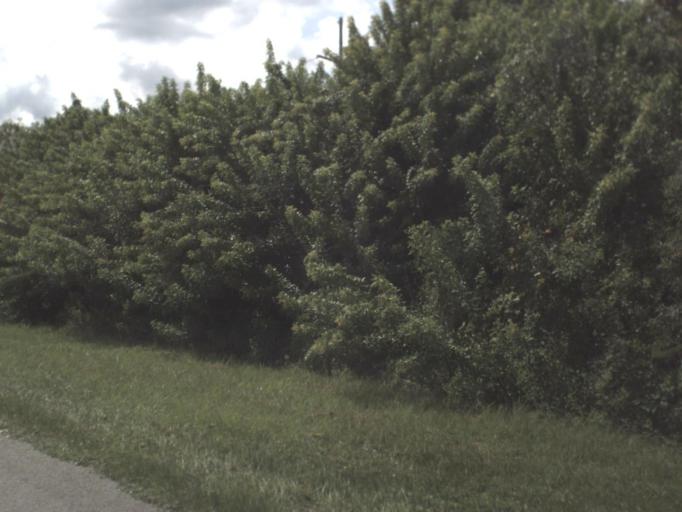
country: US
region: Florida
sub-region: Collier County
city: Immokalee
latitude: 26.2765
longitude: -81.3423
